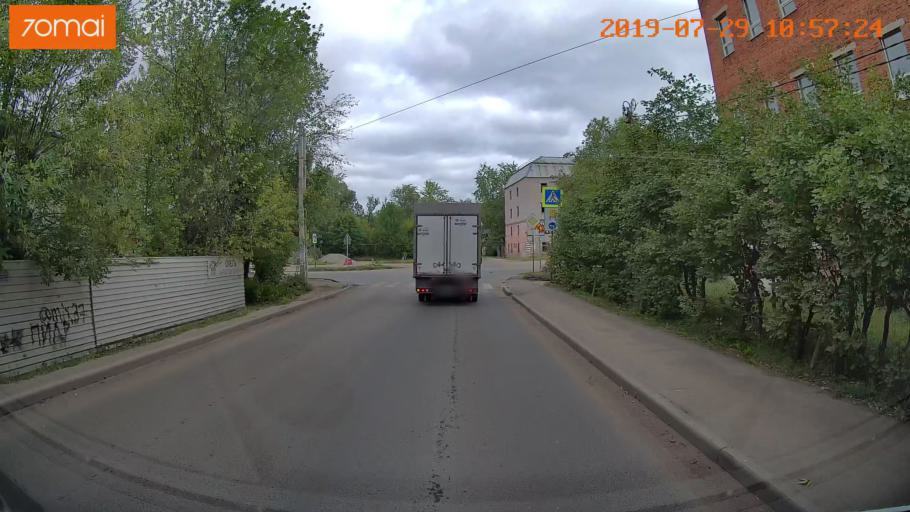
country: RU
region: Ivanovo
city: Bogorodskoye
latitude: 56.9889
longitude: 41.0365
